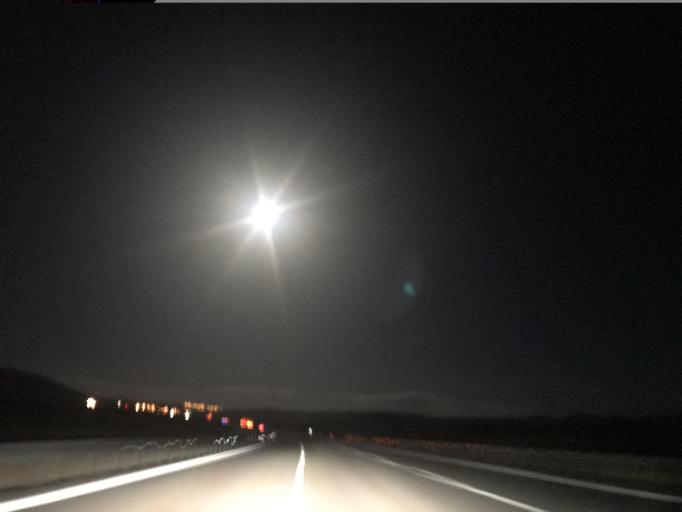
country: TR
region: Nigde
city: Ulukisla
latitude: 37.6301
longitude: 34.4624
